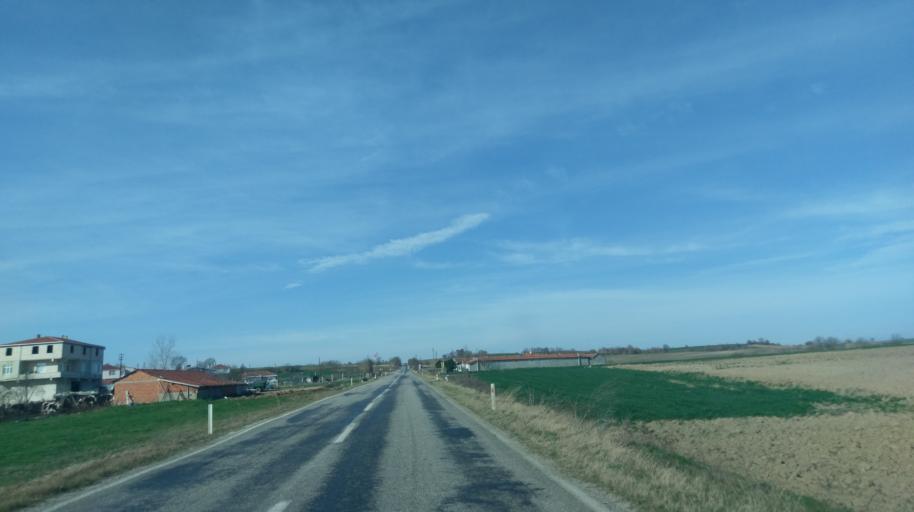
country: TR
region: Edirne
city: Copkoy
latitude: 41.2741
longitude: 26.7937
